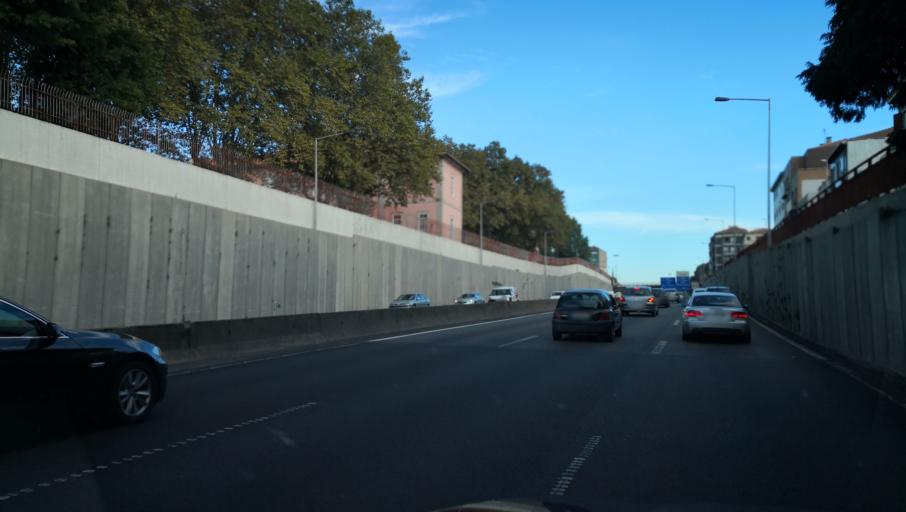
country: PT
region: Porto
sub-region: Maia
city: Pedroucos
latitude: 41.1704
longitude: -8.5928
